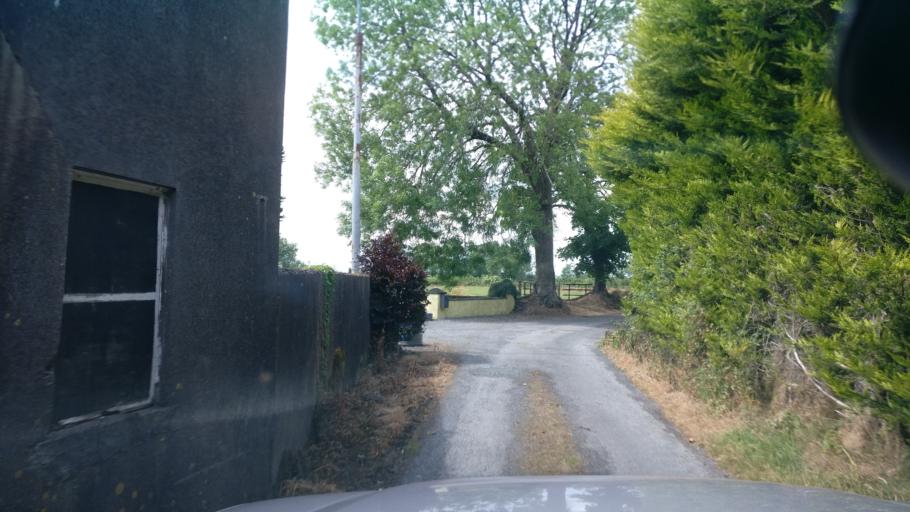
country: IE
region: Connaught
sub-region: County Galway
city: Ballinasloe
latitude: 53.2723
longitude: -8.3345
